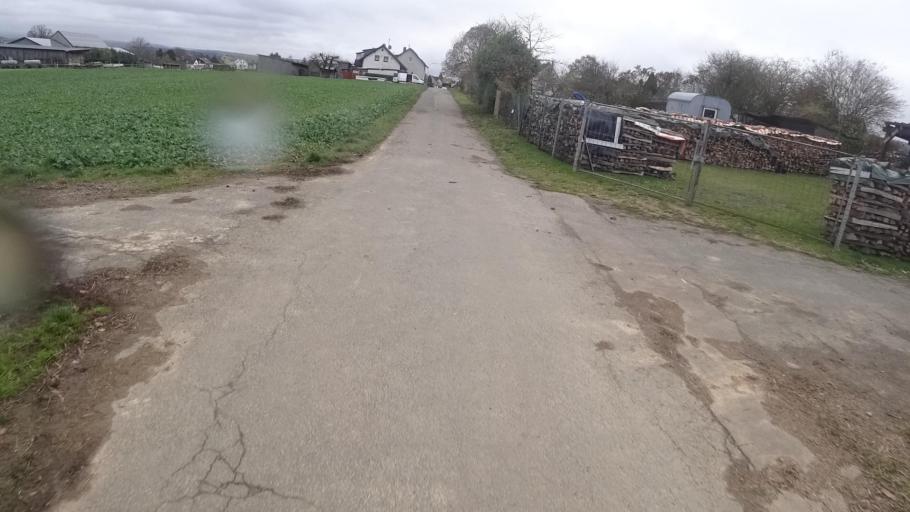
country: DE
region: Rheinland-Pfalz
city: Prath
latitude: 50.1596
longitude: 7.6836
